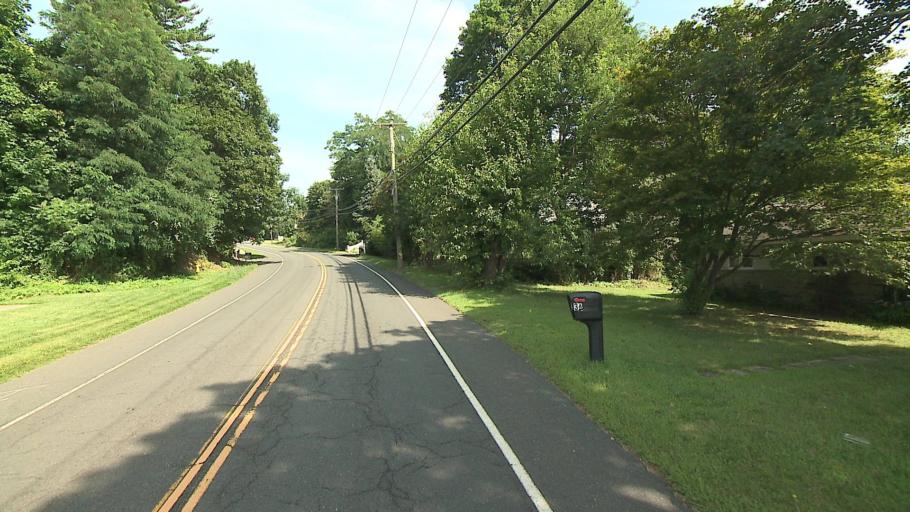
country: US
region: Connecticut
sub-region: Fairfield County
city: Danbury
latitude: 41.4081
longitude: -73.4671
